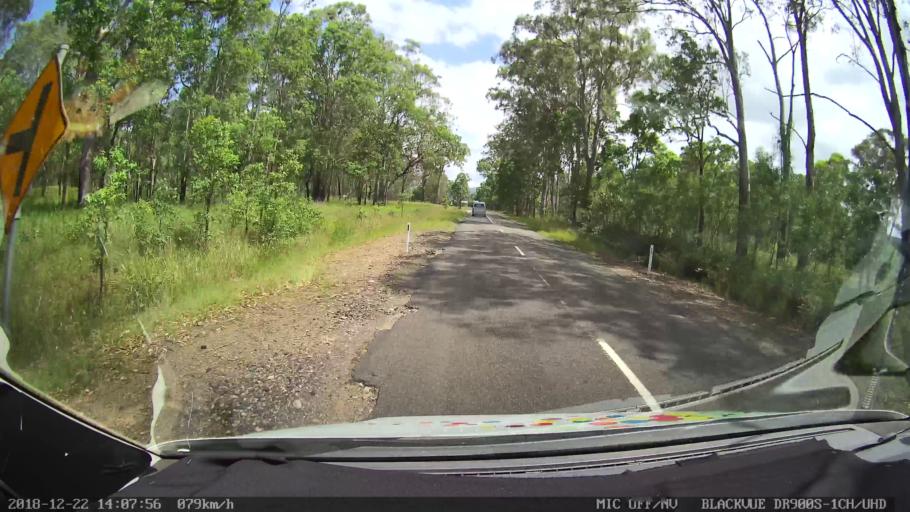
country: AU
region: New South Wales
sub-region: Clarence Valley
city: Coutts Crossing
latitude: -29.9729
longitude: 152.7261
